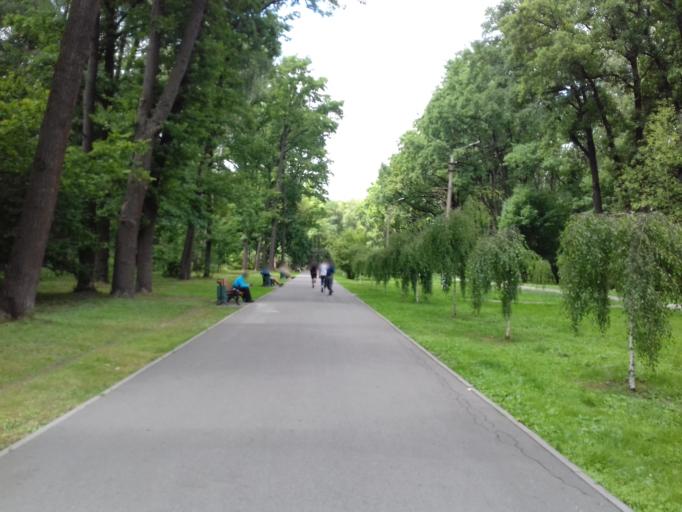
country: RU
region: Tula
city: Tula
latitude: 54.1852
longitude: 37.5914
